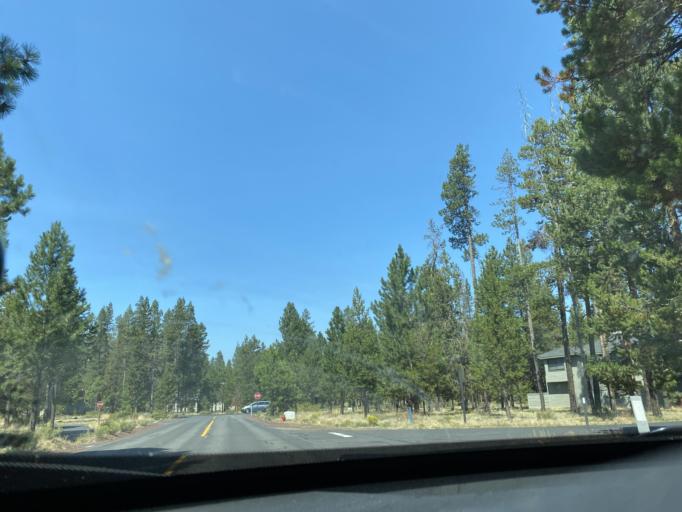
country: US
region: Oregon
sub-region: Deschutes County
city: Sunriver
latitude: 43.8931
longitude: -121.4213
